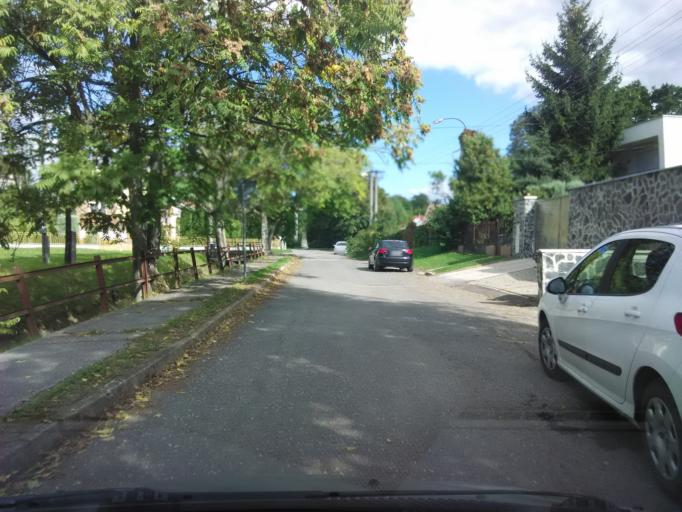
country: SK
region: Nitriansky
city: Levice
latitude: 48.2107
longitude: 18.6251
